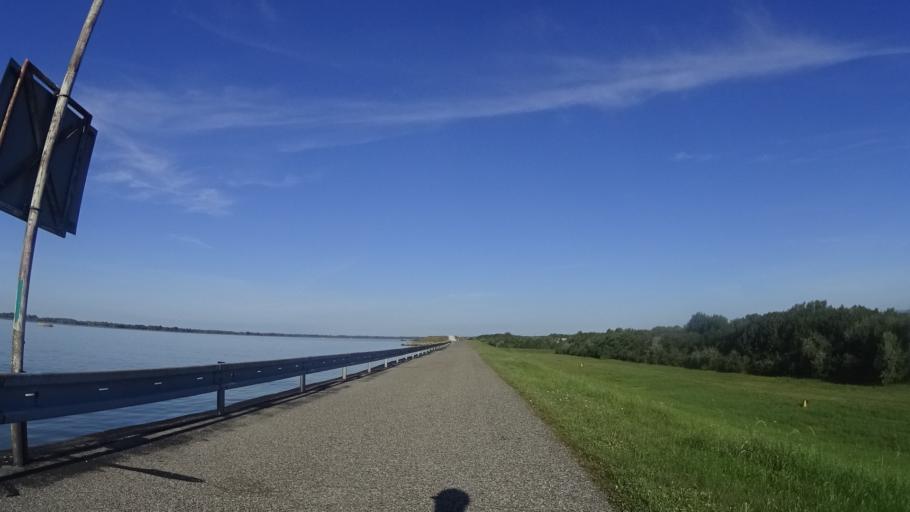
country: SK
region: Trnavsky
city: Samorin
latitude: 48.0064
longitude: 17.3240
